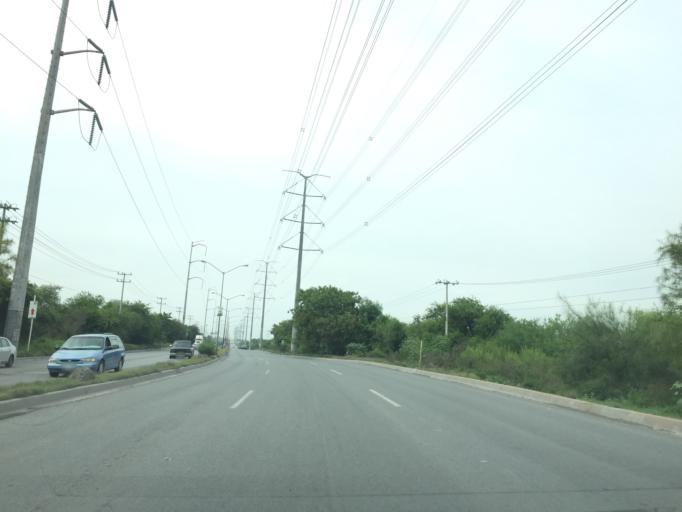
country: MX
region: Nuevo Leon
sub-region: Apodaca
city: Fraccionamiento Cosmopolis Octavo Sector
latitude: 25.7883
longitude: -100.2233
